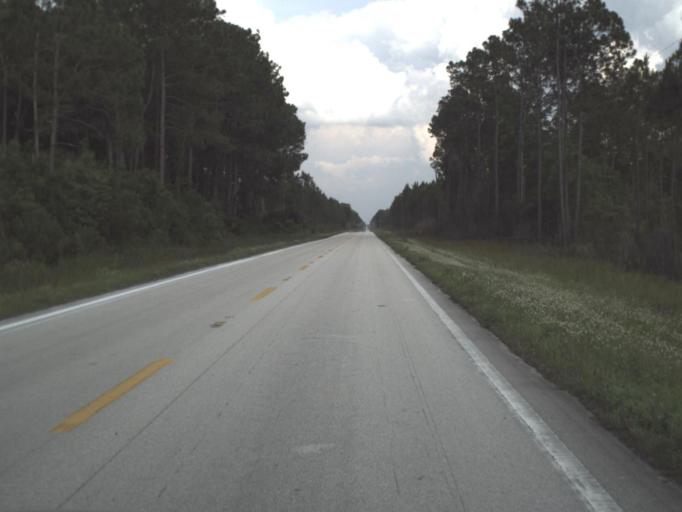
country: US
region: Florida
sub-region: Baker County
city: Macclenny
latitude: 30.5338
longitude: -82.3193
